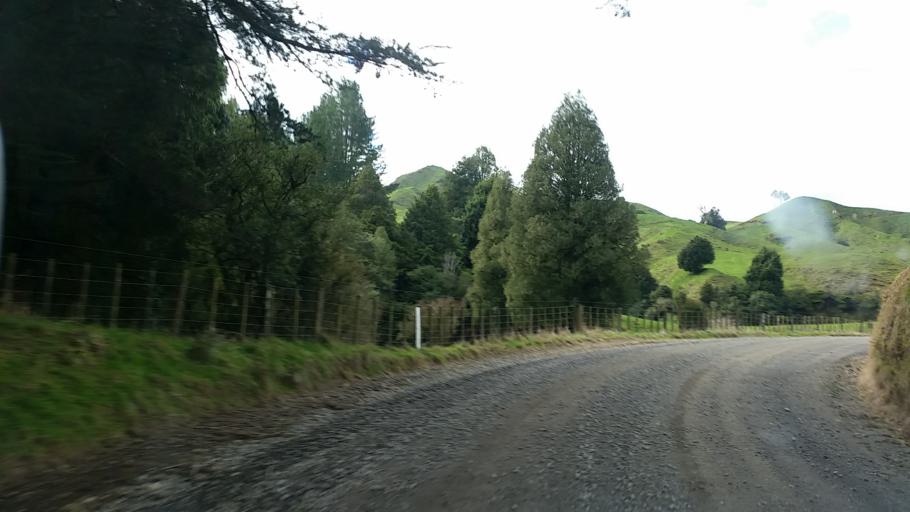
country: NZ
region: Taranaki
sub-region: New Plymouth District
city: Waitara
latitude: -39.1606
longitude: 174.5874
